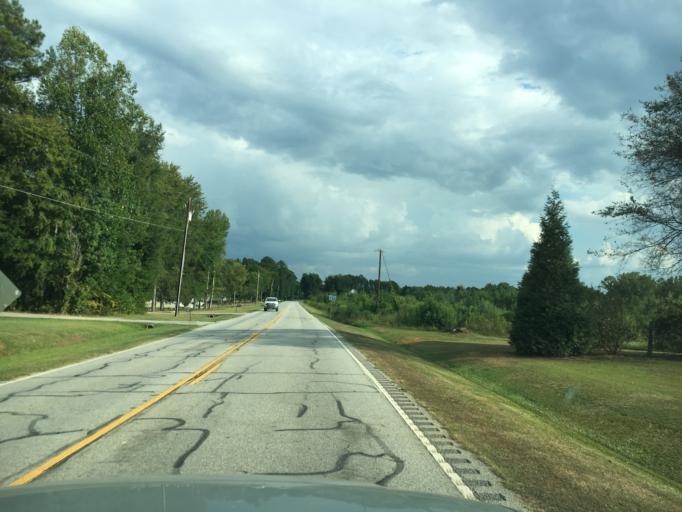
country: US
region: South Carolina
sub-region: Greenwood County
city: Ninety Six
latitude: 34.2071
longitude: -82.0338
